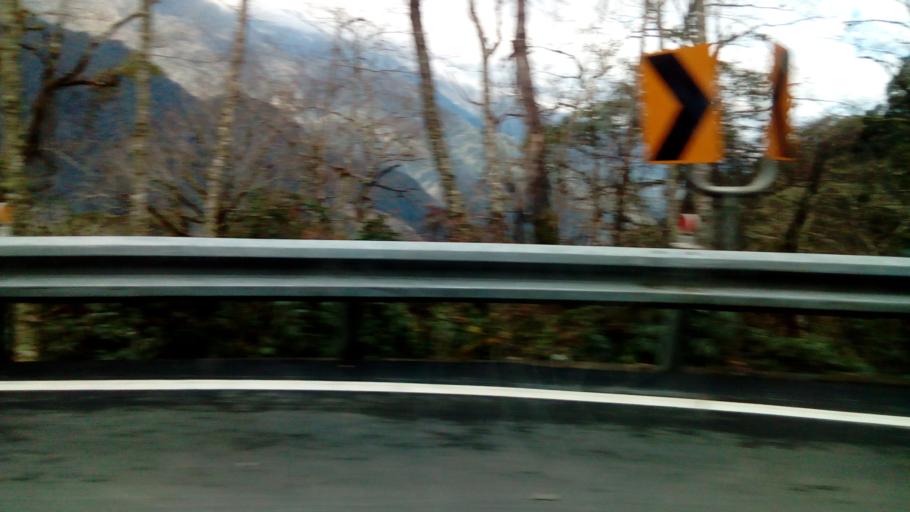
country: TW
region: Taiwan
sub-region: Hualien
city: Hualian
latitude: 24.3987
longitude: 121.3694
